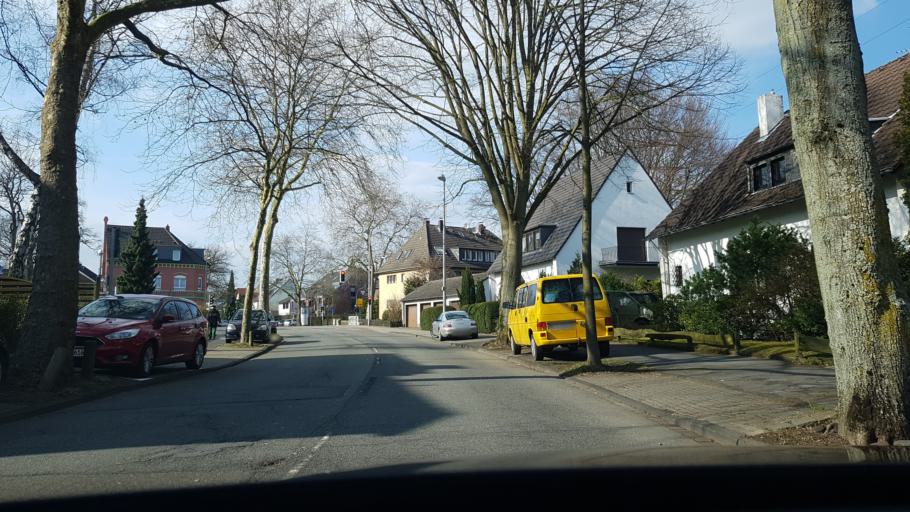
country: DE
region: North Rhine-Westphalia
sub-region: Regierungsbezirk Dusseldorf
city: Muelheim (Ruhr)
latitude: 51.4092
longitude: 6.8547
